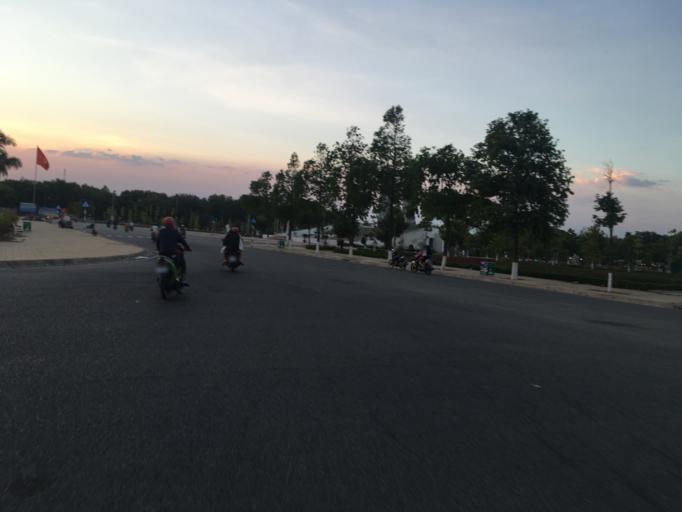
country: VN
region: Ninh Thuan
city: Phan Rang-Thap Cham
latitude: 11.5653
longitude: 109.0011
